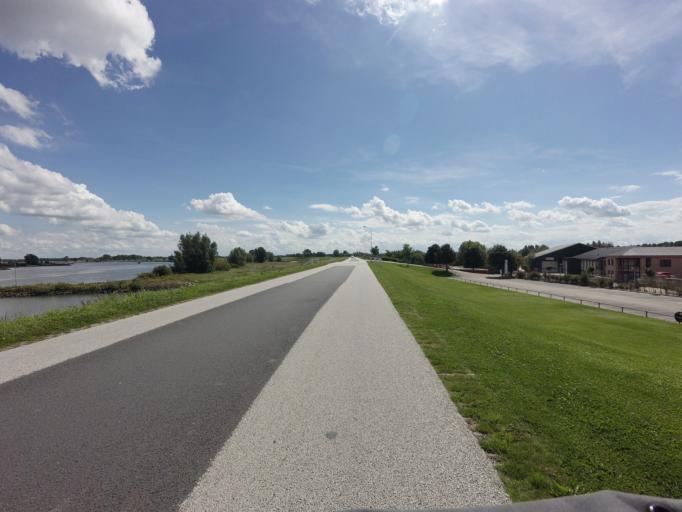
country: NL
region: Utrecht
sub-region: Gemeente IJsselstein
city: IJsselstein
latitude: 51.9716
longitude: 5.0134
